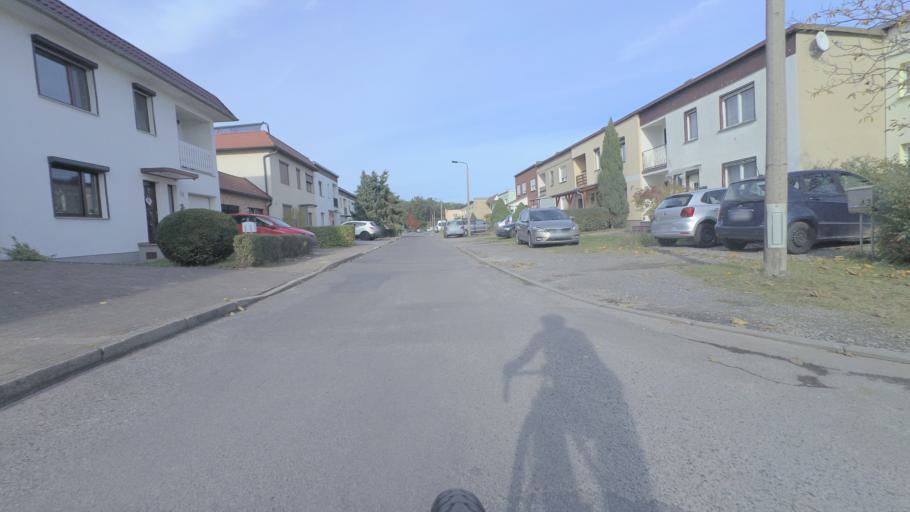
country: DE
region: Brandenburg
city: Ludwigsfelde
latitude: 52.2956
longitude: 13.2459
